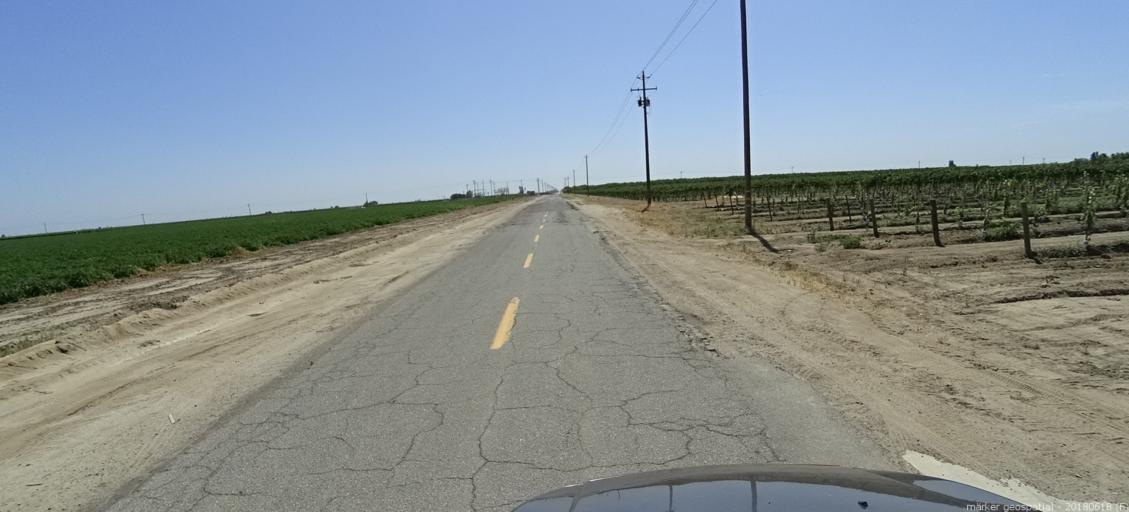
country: US
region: California
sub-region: Madera County
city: Parkwood
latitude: 36.8803
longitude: -120.1698
